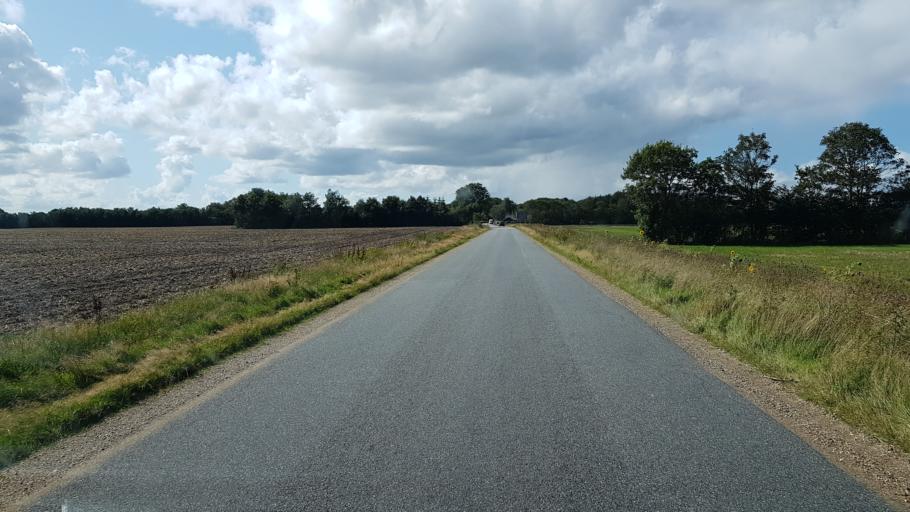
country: DK
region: South Denmark
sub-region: Esbjerg Kommune
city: Bramming
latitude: 55.6170
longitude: 8.7346
